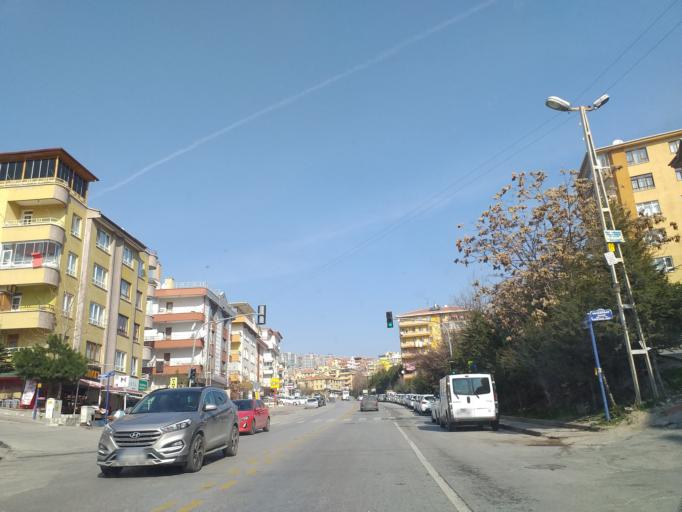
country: TR
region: Ankara
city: Ankara
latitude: 39.9938
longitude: 32.8558
